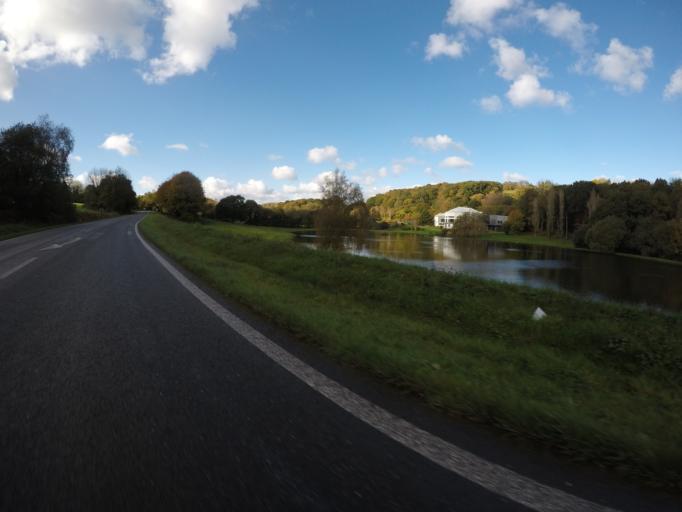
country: FR
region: Brittany
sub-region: Departement des Cotes-d'Armor
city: Bourbriac
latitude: 48.4881
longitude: -3.1806
